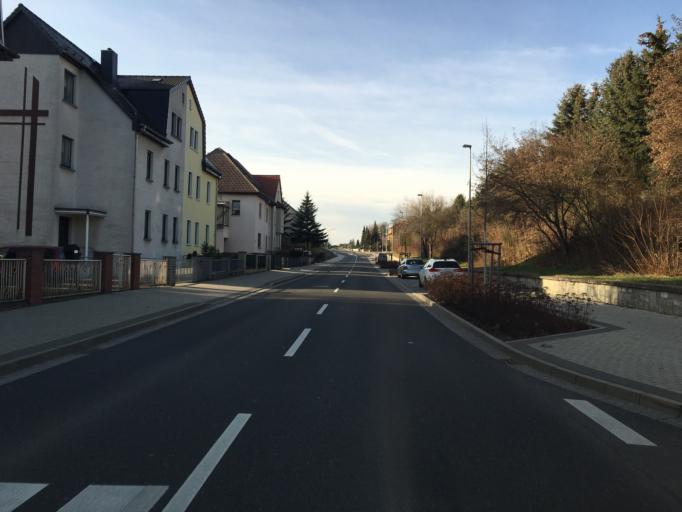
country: DE
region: Saxony
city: Oschatz
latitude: 51.2961
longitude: 13.0992
